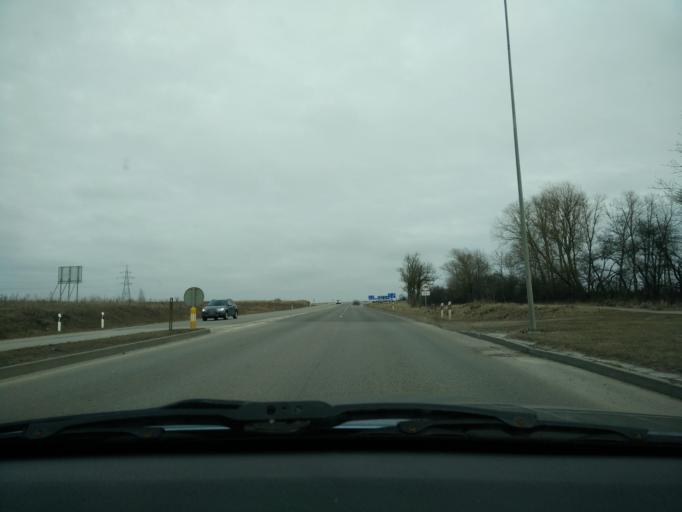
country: LT
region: Klaipedos apskritis
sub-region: Klaipeda
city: Klaipeda
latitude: 55.7290
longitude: 21.1783
